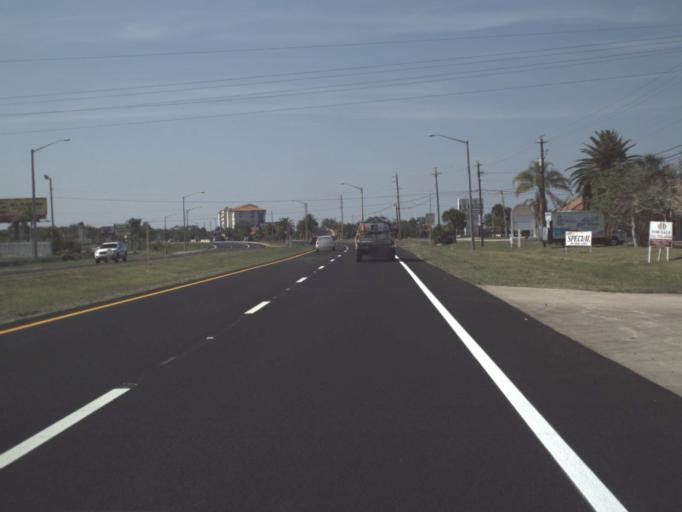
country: US
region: Florida
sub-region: Brevard County
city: Titusville
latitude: 28.5499
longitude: -80.7958
